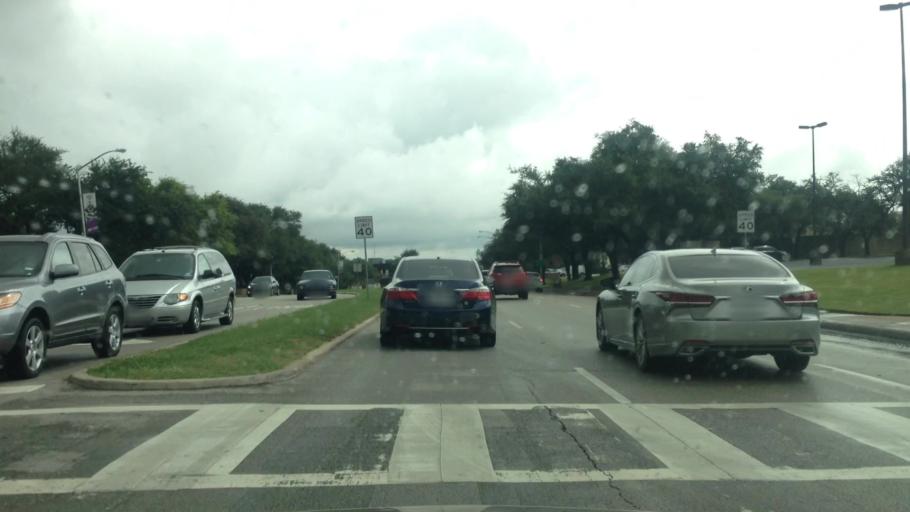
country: US
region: Texas
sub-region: Tarrant County
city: Edgecliff Village
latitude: 32.6852
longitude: -97.3924
